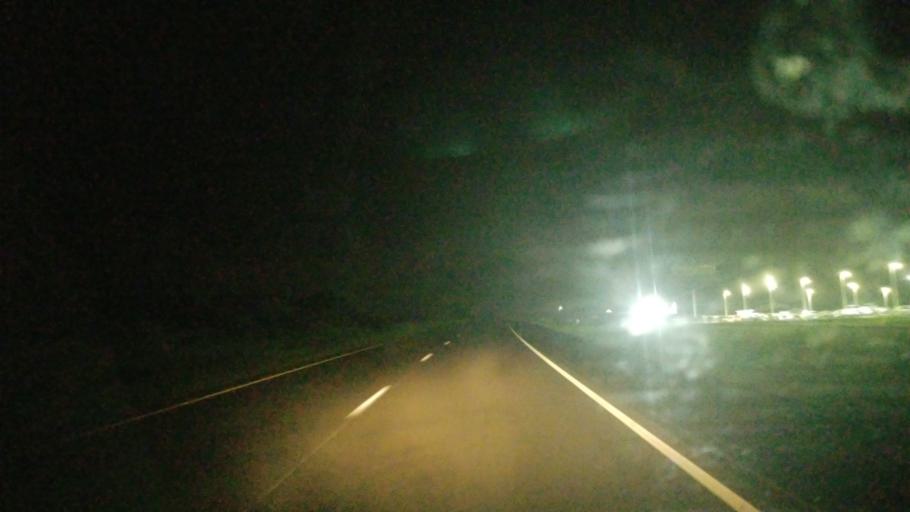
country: US
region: Missouri
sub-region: Lincoln County
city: Moscow Mills
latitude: 38.9521
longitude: -90.9352
